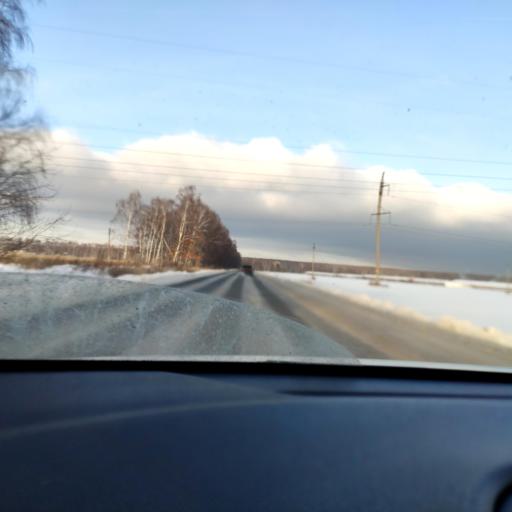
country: RU
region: Tatarstan
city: Osinovo
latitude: 55.8891
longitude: 48.8907
